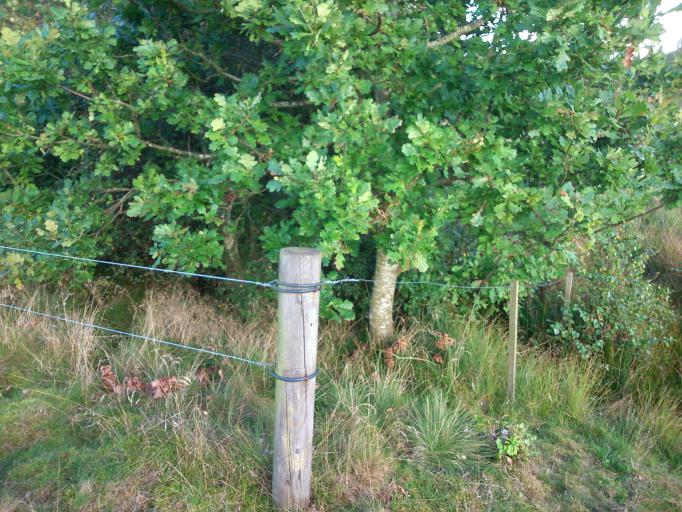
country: DK
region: Central Jutland
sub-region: Ringkobing-Skjern Kommune
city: Tarm
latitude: 55.9441
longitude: 8.5836
